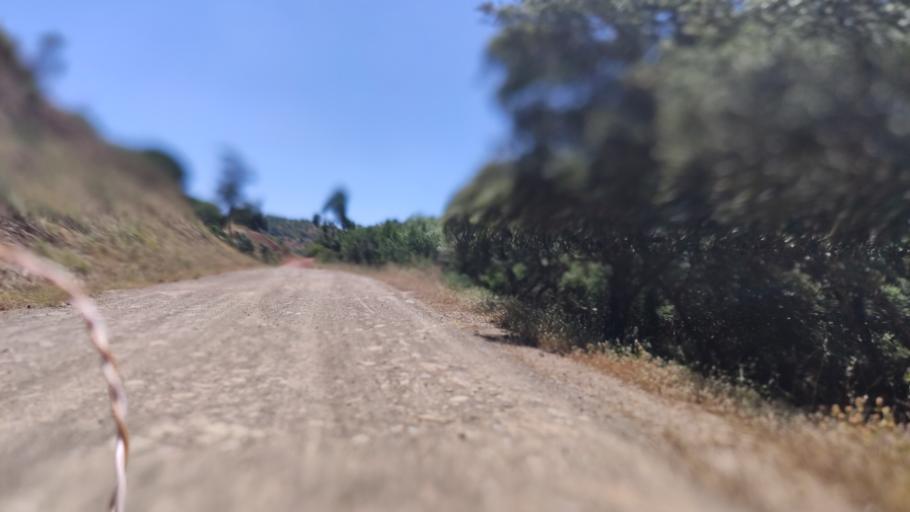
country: PT
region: Faro
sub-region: Sao Bras de Alportel
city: Sao Bras de Alportel
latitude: 37.1756
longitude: -7.9309
